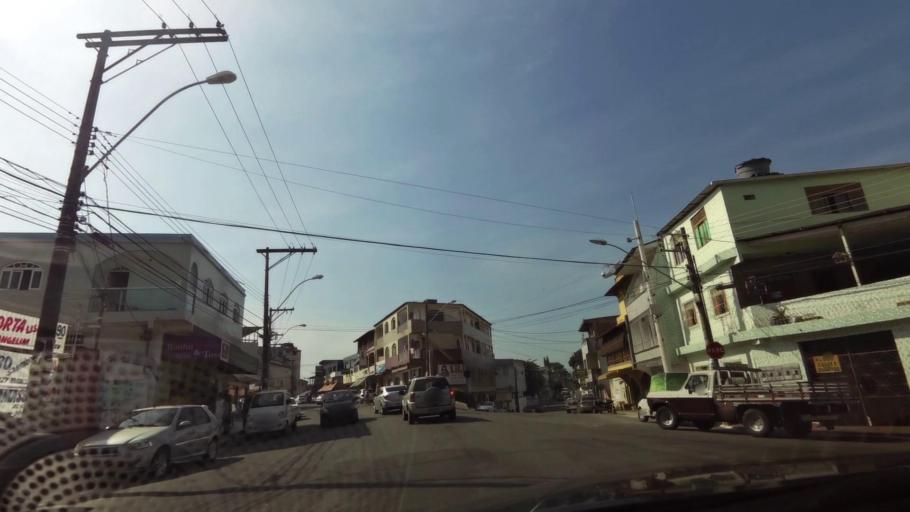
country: BR
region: Espirito Santo
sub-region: Guarapari
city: Guarapari
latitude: -20.6567
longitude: -40.4963
